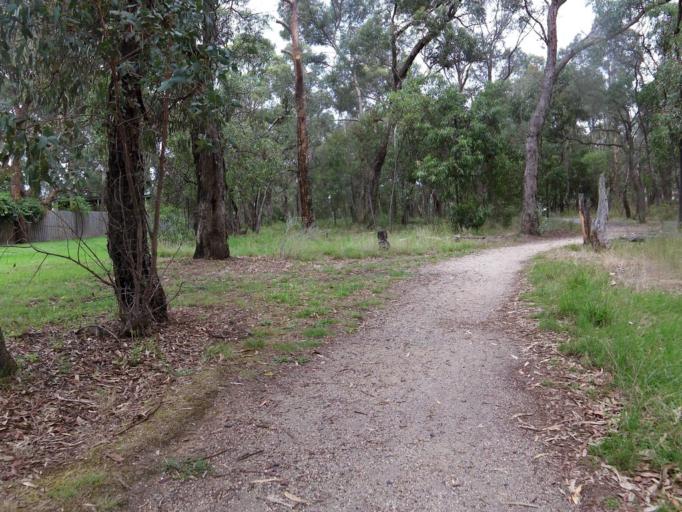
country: AU
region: Victoria
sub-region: Whitehorse
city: Forest Hill
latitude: -37.8292
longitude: 145.1642
